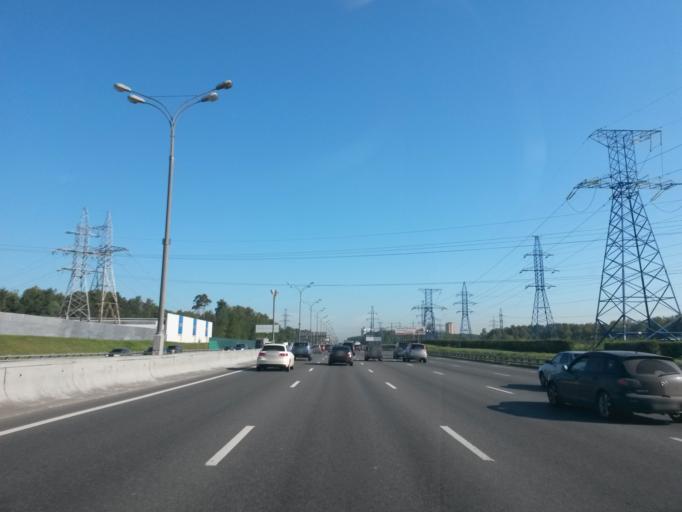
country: RU
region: Moscow
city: Ivanovskoye
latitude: 55.7820
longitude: 37.8423
